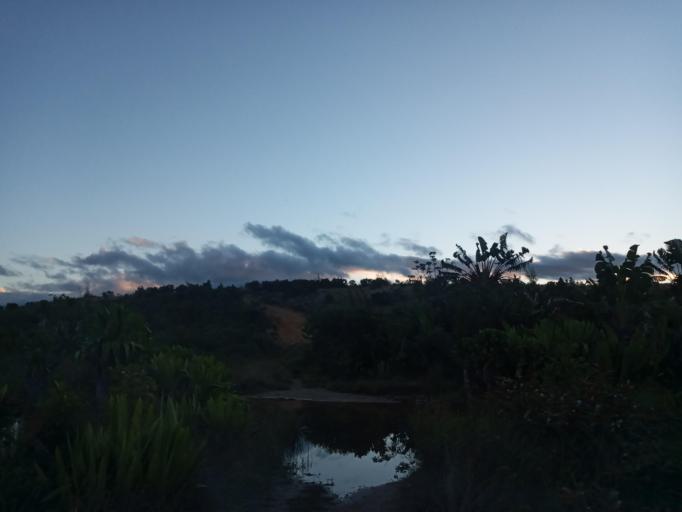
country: MG
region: Anosy
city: Fort Dauphin
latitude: -24.5110
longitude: 47.2255
